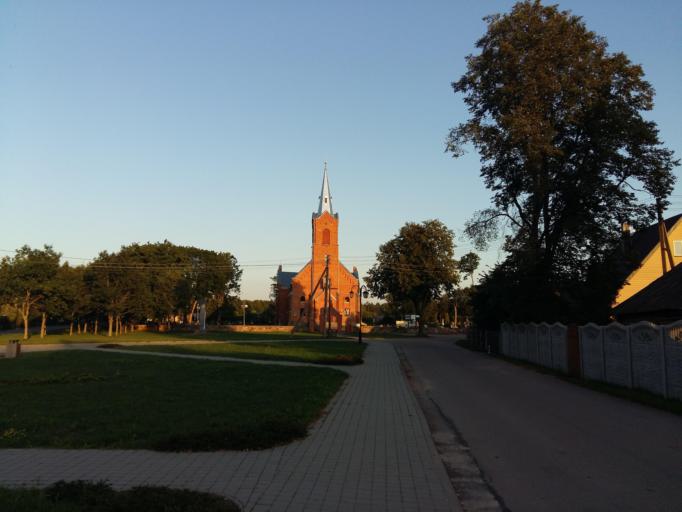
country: LT
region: Alytaus apskritis
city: Varena
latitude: 54.2152
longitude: 24.4171
